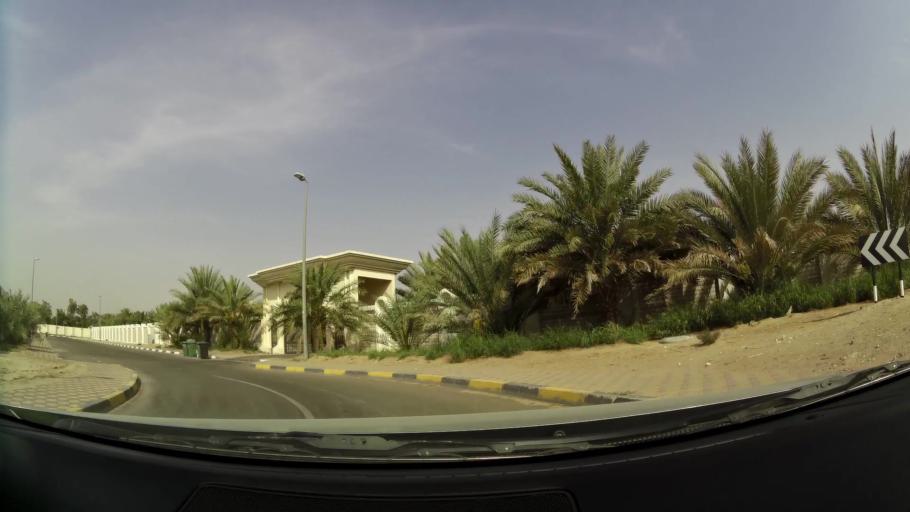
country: AE
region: Abu Dhabi
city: Al Ain
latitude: 24.1434
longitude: 55.6946
